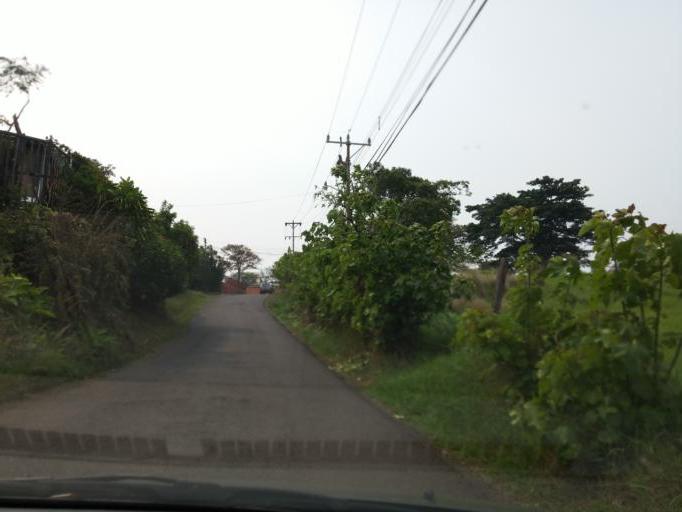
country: CR
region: Alajuela
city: Alajuela
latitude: 9.9928
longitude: -84.2302
